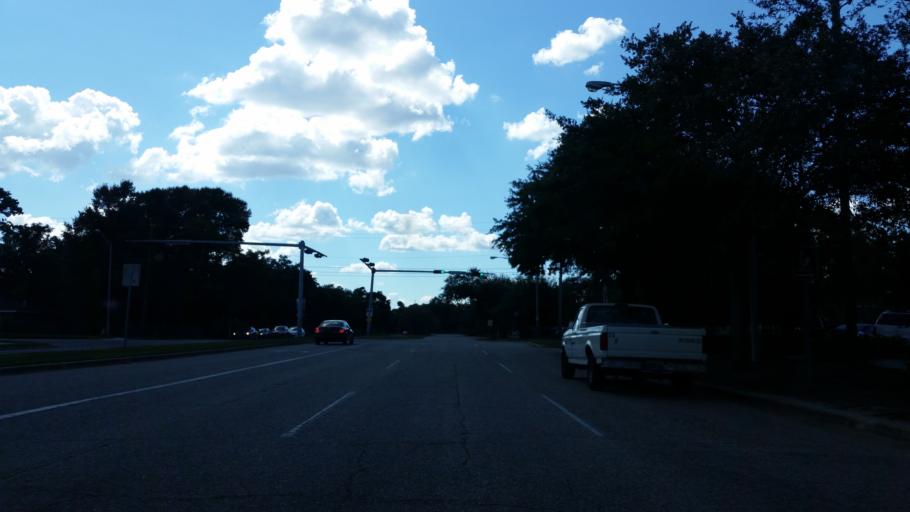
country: US
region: Alabama
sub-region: Mobile County
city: Mobile
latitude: 30.6839
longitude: -88.0483
